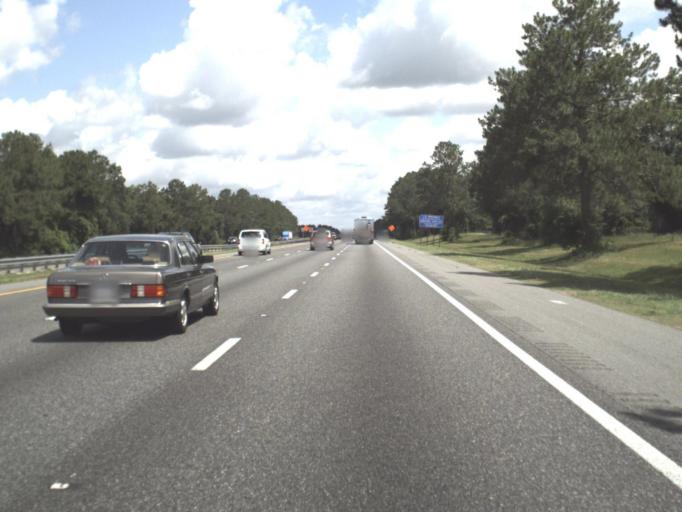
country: US
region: Florida
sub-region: Columbia County
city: Lake City
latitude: 30.0988
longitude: -82.6447
